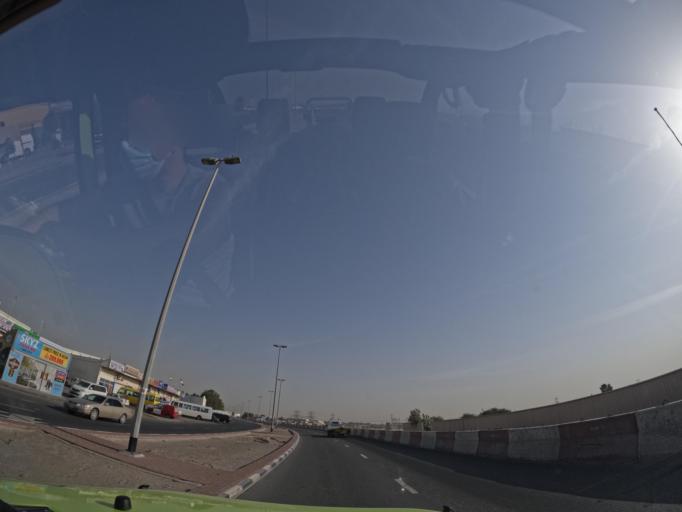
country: AE
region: Ash Shariqah
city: Sharjah
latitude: 25.1803
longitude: 55.3293
